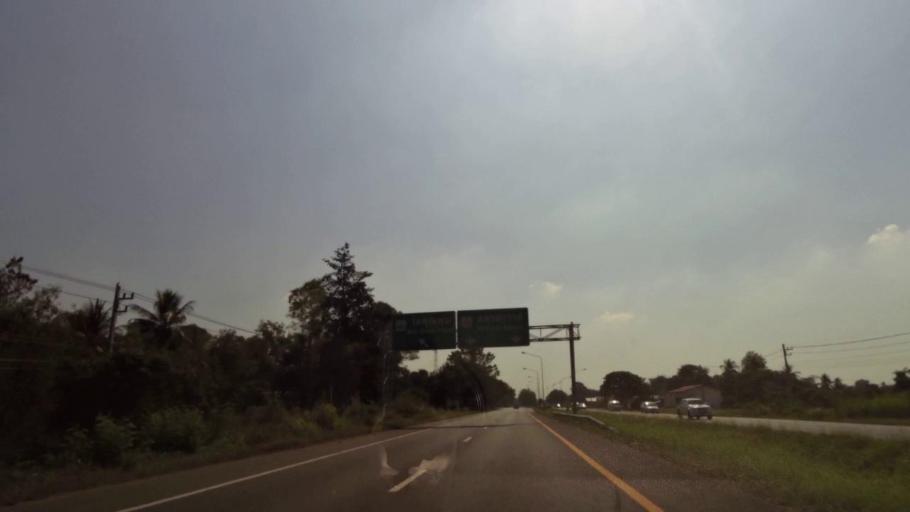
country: TH
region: Phichit
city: Bueng Na Rang
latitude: 16.1960
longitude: 100.1283
